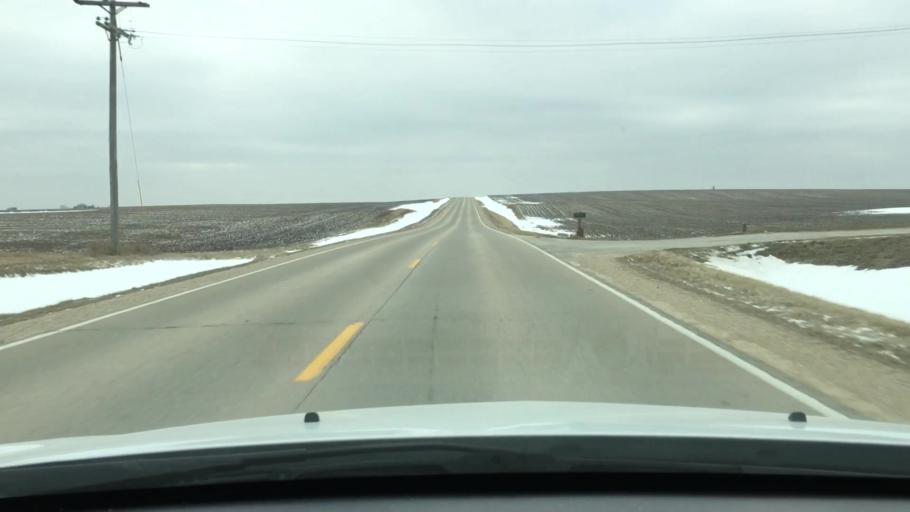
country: US
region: Illinois
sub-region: DeKalb County
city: Malta
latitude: 41.8480
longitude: -88.9449
